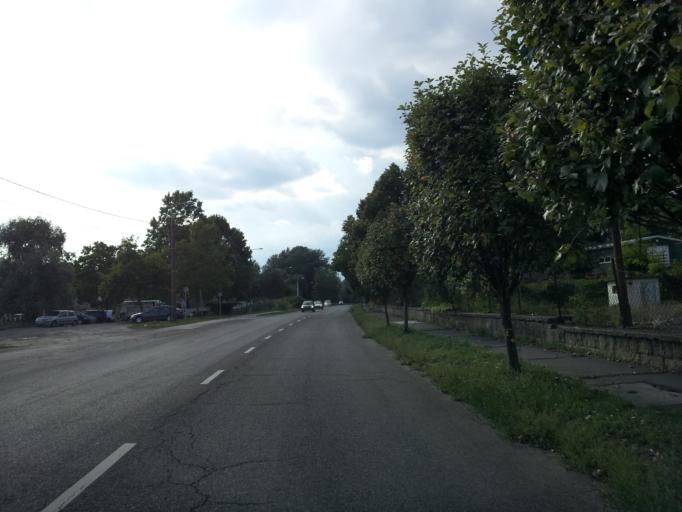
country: HU
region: Pest
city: Veroce
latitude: 47.8227
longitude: 19.0263
